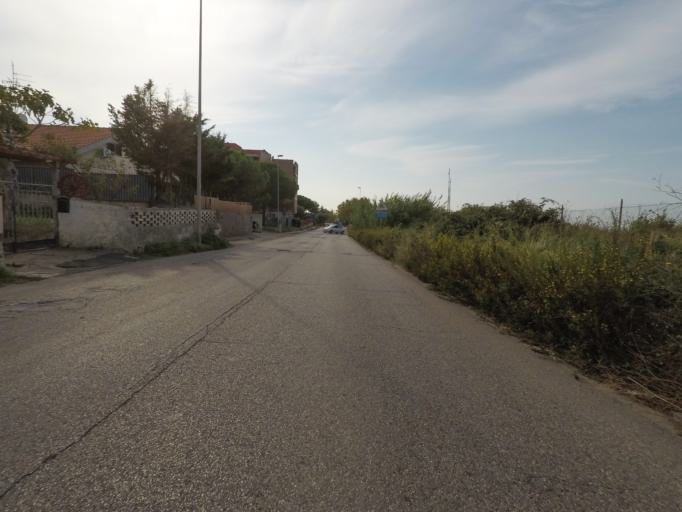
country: IT
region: Latium
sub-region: Citta metropolitana di Roma Capitale
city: Civitavecchia
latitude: 42.1038
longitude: 11.8101
